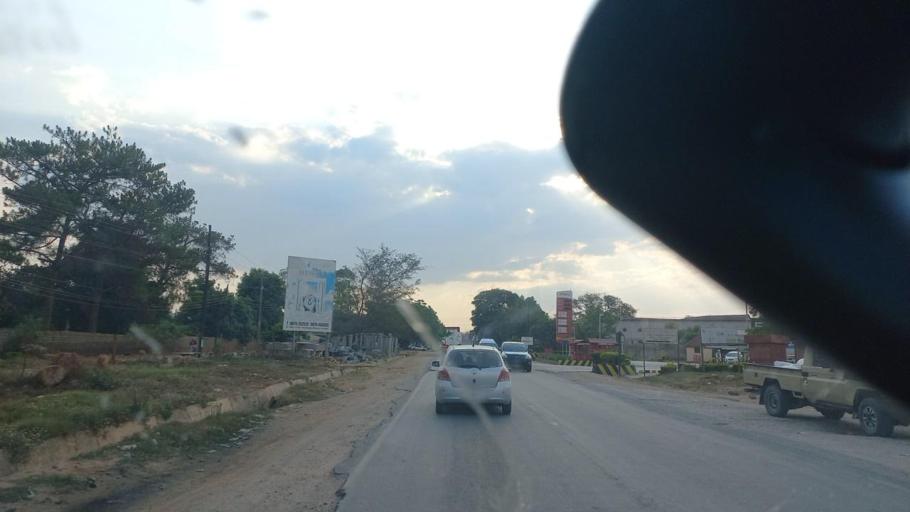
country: ZM
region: Lusaka
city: Lusaka
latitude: -15.3699
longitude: 28.4050
